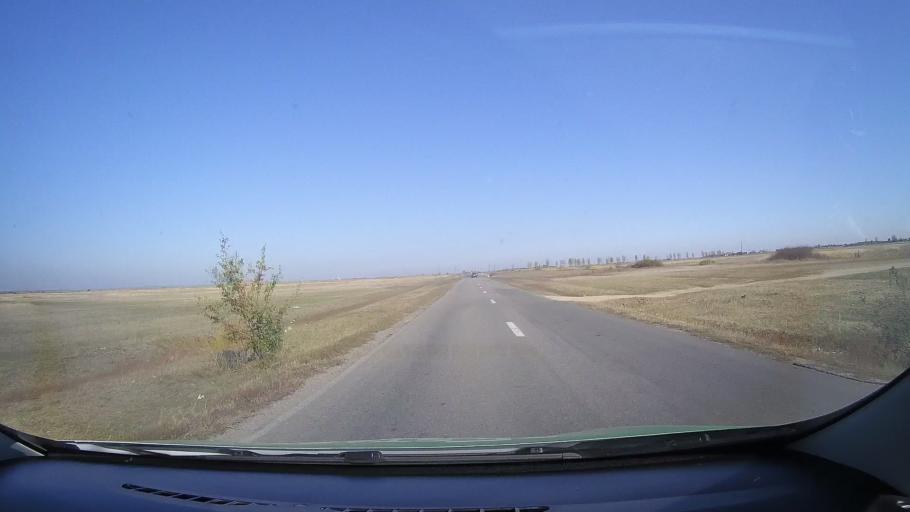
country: RO
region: Satu Mare
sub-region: Comuna Cauas
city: Cauas
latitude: 47.5888
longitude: 22.5470
